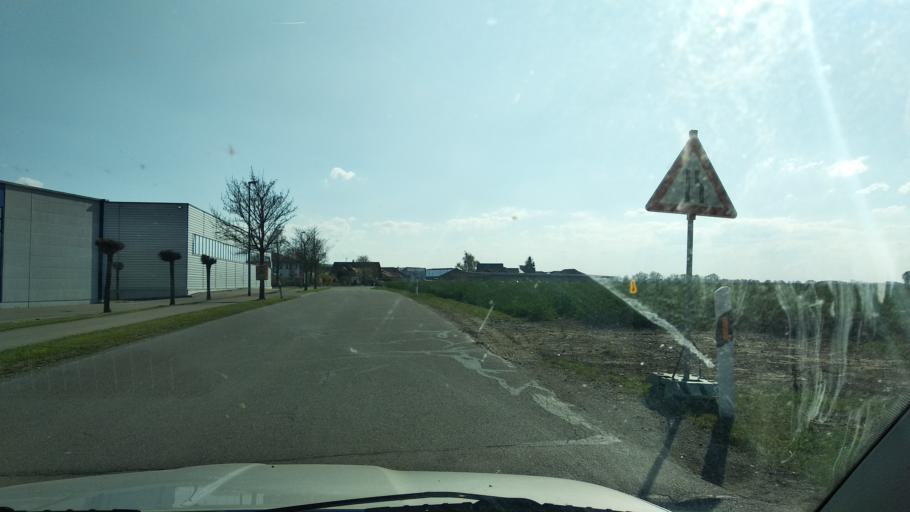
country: DE
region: Bavaria
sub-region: Swabia
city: Hawangen
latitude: 47.9691
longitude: 10.2585
